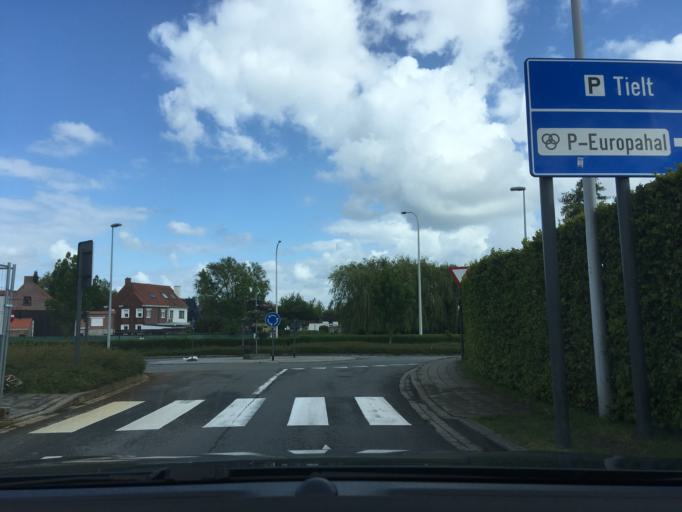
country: BE
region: Flanders
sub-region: Provincie West-Vlaanderen
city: Tielt
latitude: 51.0040
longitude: 3.3269
